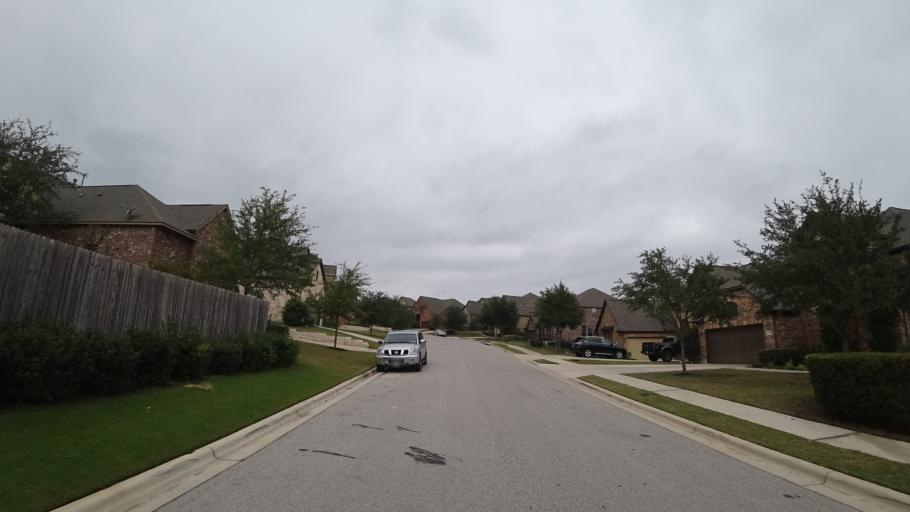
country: US
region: Texas
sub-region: Travis County
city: Bee Cave
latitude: 30.3427
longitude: -97.9075
